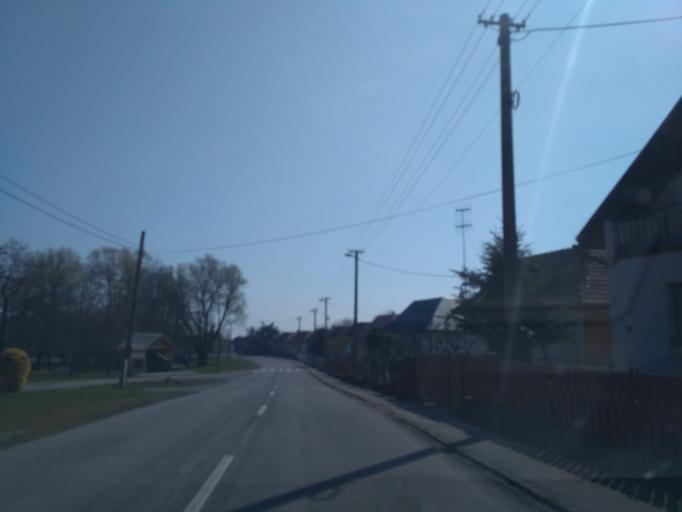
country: SK
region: Kosicky
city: Secovce
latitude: 48.7386
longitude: 21.6267
